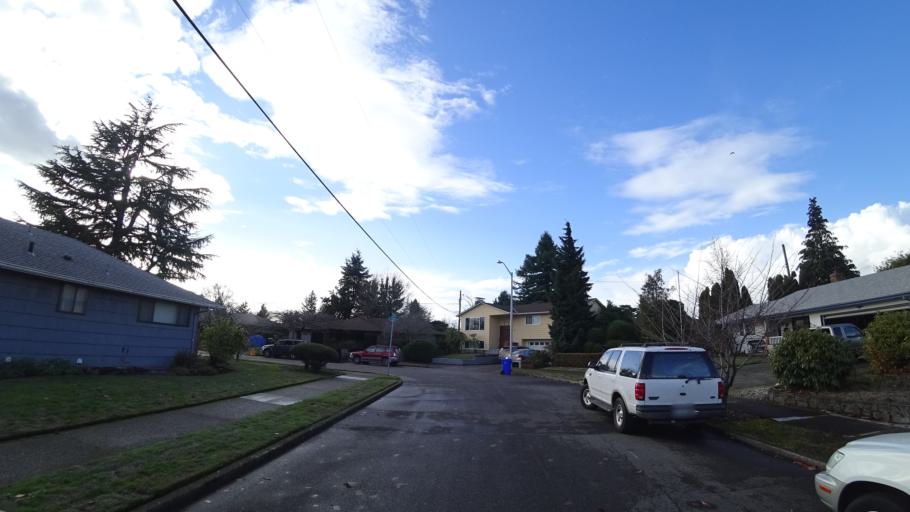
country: US
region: Oregon
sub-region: Multnomah County
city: Lents
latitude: 45.5254
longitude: -122.5511
